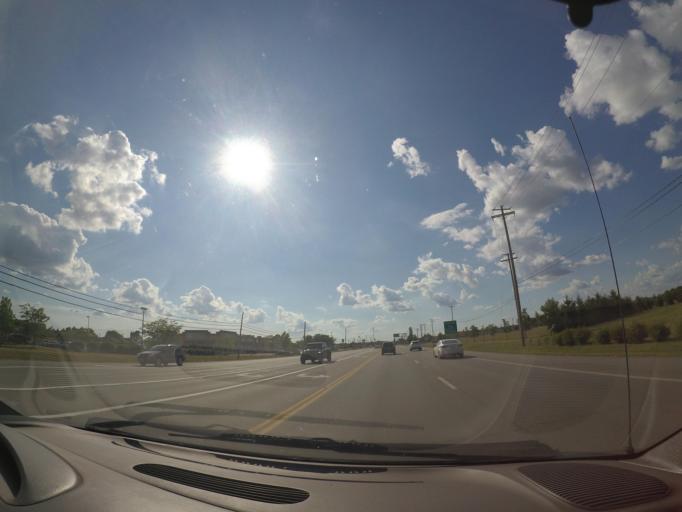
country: US
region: Ohio
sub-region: Wood County
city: Perrysburg
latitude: 41.5457
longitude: -83.5923
